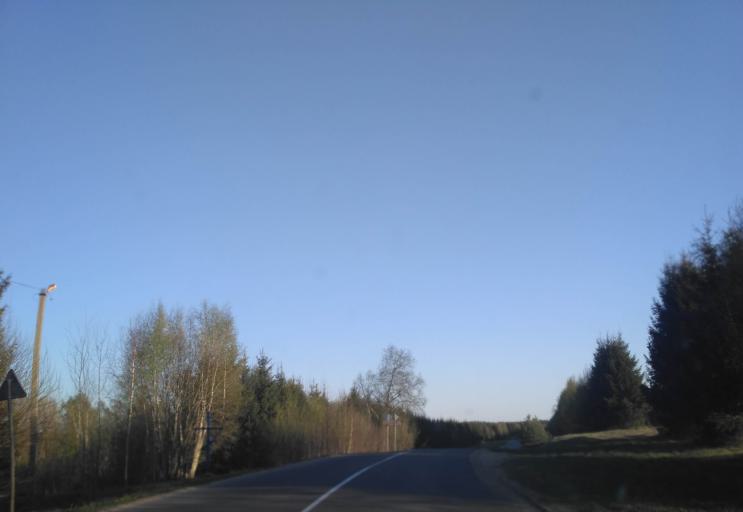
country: BY
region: Minsk
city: Radashkovichy
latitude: 54.1284
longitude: 27.2006
